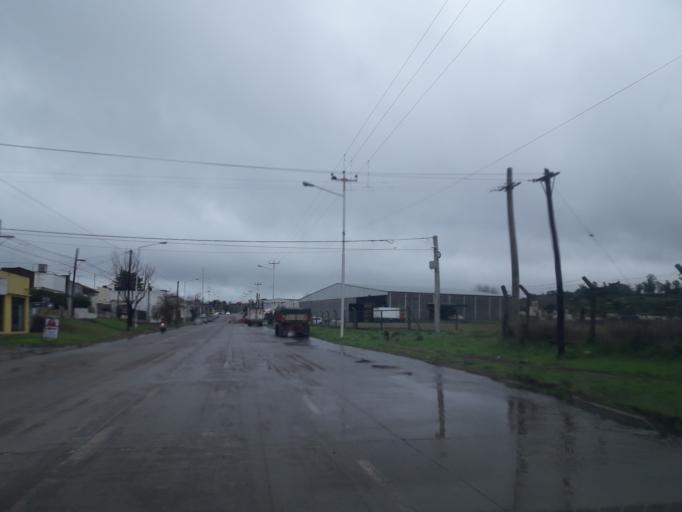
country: AR
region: Buenos Aires
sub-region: Partido de Tandil
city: Tandil
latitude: -37.3185
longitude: -59.1585
